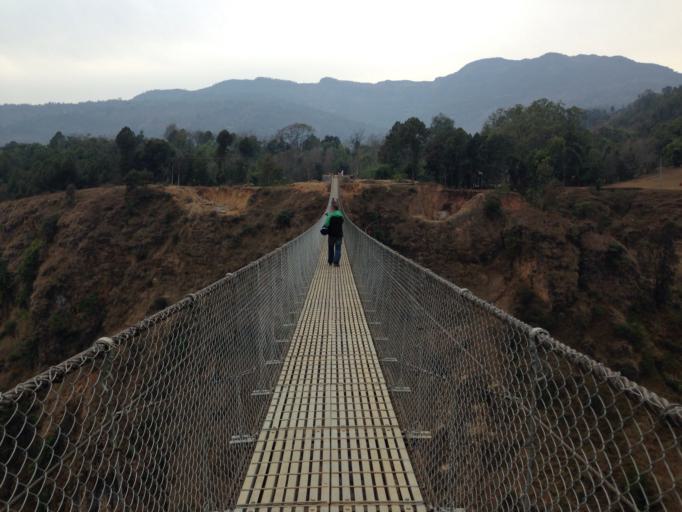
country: NP
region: Western Region
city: Baglung
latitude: 28.2048
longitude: 83.6709
